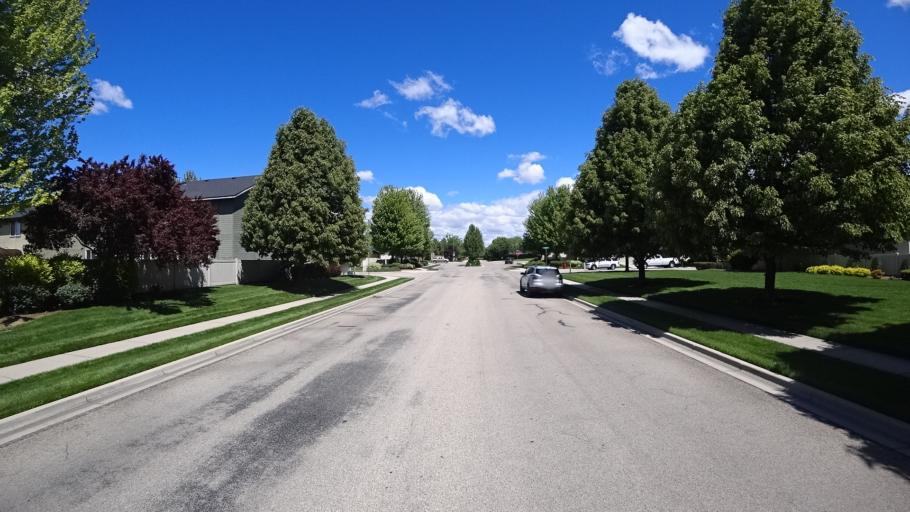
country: US
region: Idaho
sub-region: Ada County
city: Meridian
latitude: 43.6328
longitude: -116.3430
